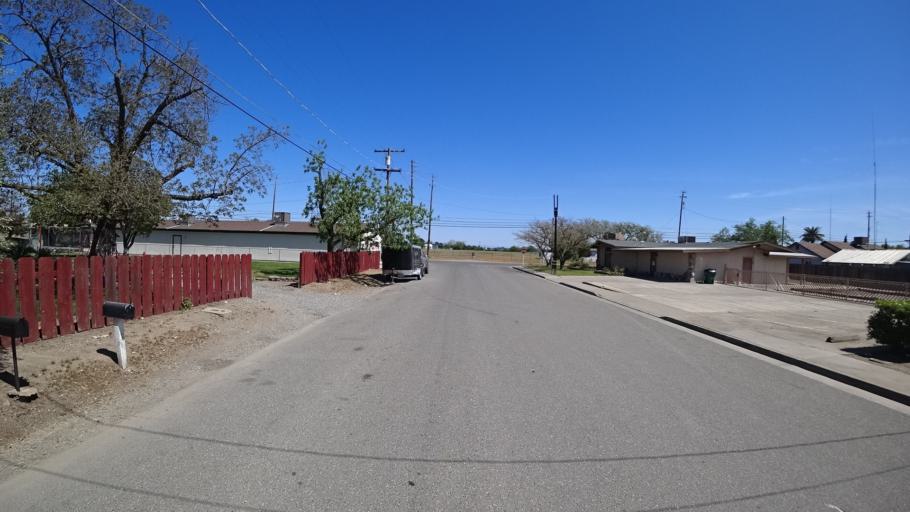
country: US
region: California
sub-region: Glenn County
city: Orland
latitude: 39.7464
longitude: -122.1789
